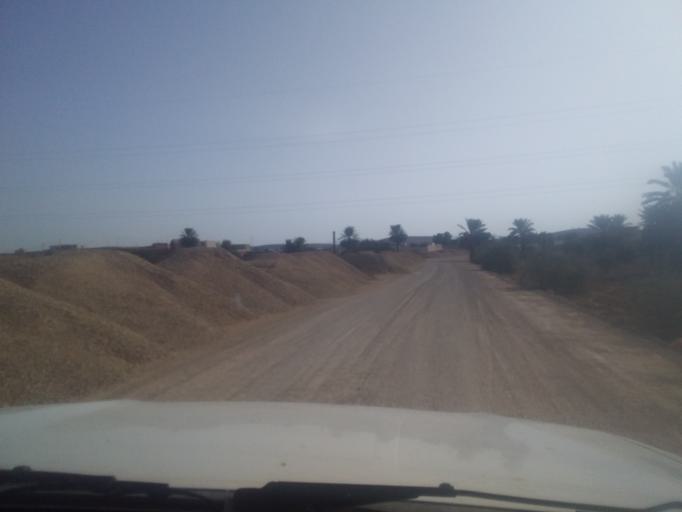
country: TN
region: Qabis
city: Matmata
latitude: 33.5870
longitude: 10.2701
